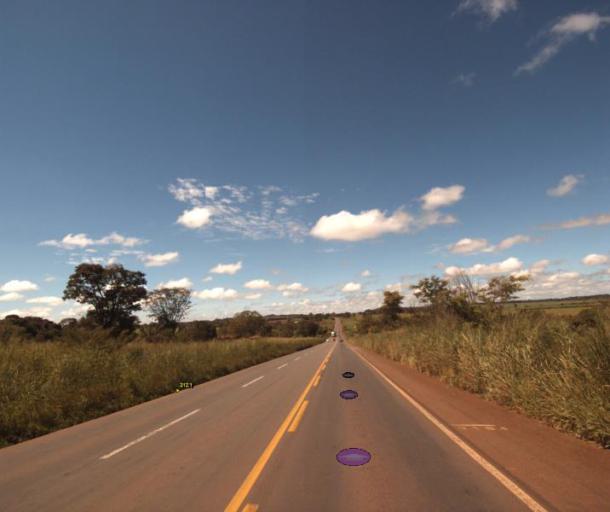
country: BR
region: Goias
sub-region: Rialma
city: Rialma
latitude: -15.3844
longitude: -49.5521
